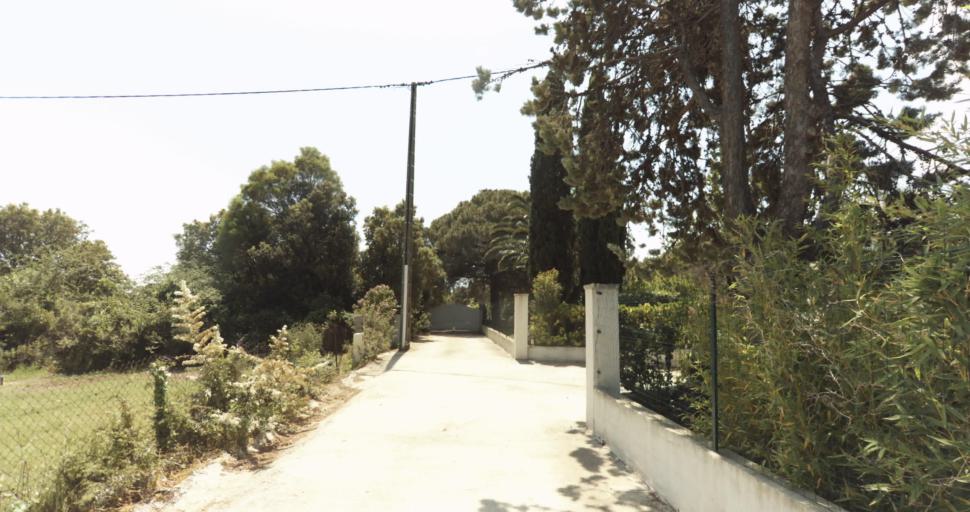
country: FR
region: Corsica
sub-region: Departement de la Haute-Corse
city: Biguglia
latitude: 42.5907
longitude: 9.4290
